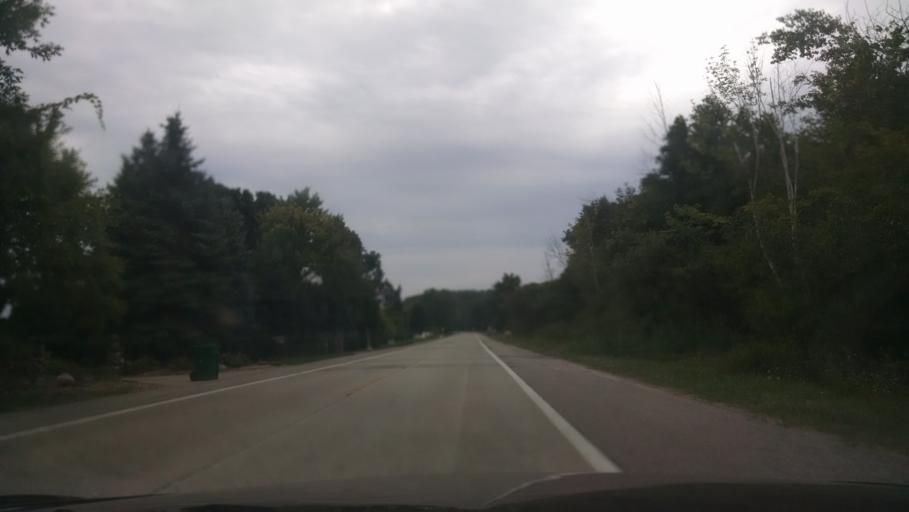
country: US
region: Michigan
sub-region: Leelanau County
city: Greilickville
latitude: 44.8767
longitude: -85.6494
